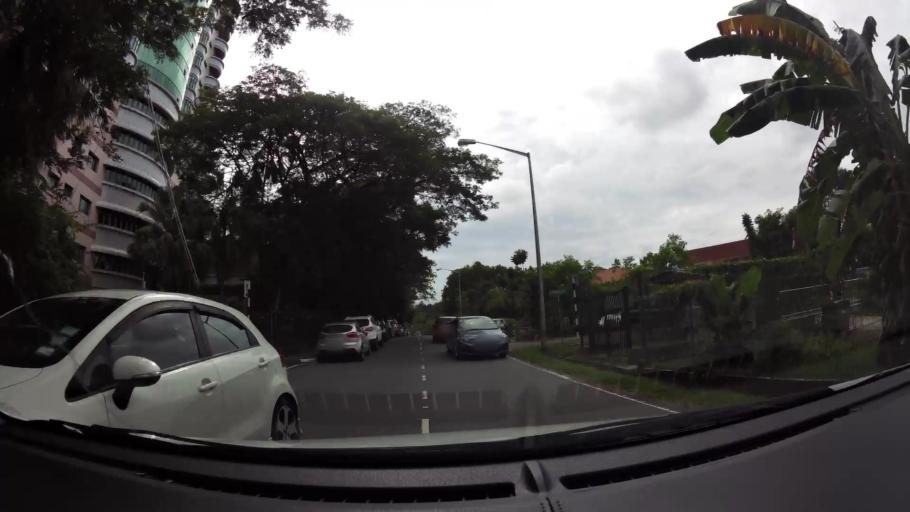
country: BN
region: Brunei and Muara
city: Bandar Seri Begawan
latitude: 4.9059
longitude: 114.9374
